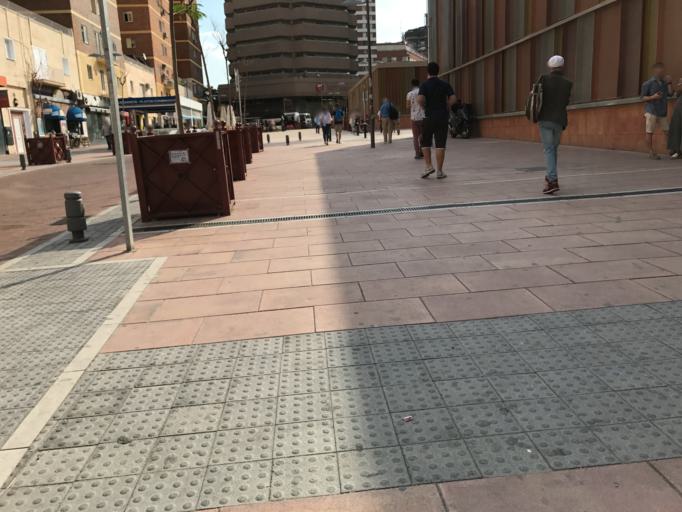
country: ES
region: Madrid
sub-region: Provincia de Madrid
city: Salamanca
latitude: 40.4385
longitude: -3.6764
